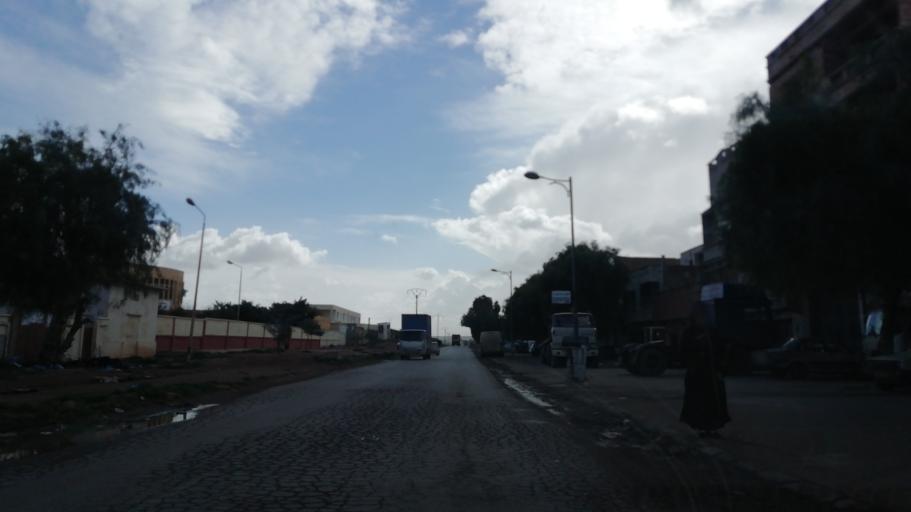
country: DZ
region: Oran
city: Sidi ech Chahmi
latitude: 35.6490
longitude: -0.5630
